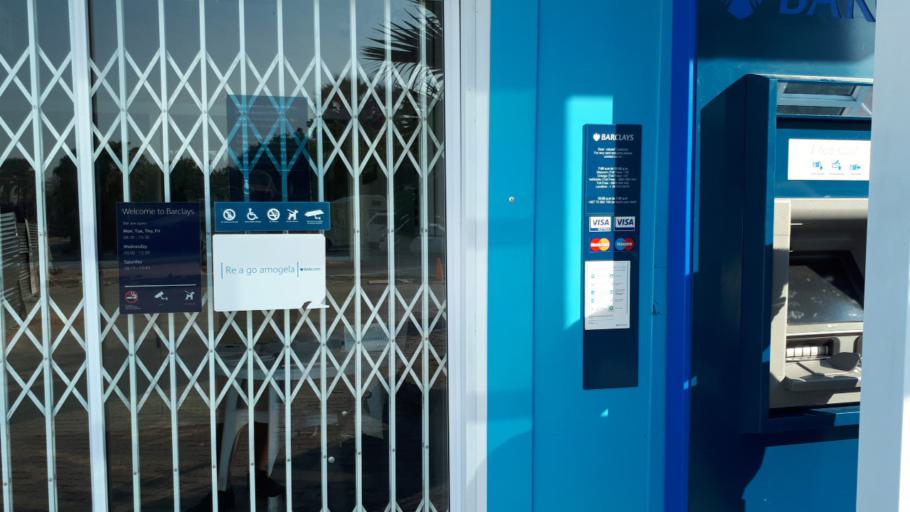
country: BW
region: Central
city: Nata
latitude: -20.2103
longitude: 26.1812
